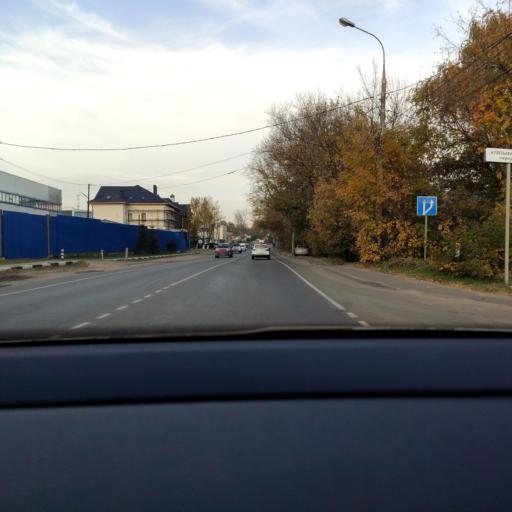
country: RU
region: Moskovskaya
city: Pirogovskiy
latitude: 55.9738
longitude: 37.7279
